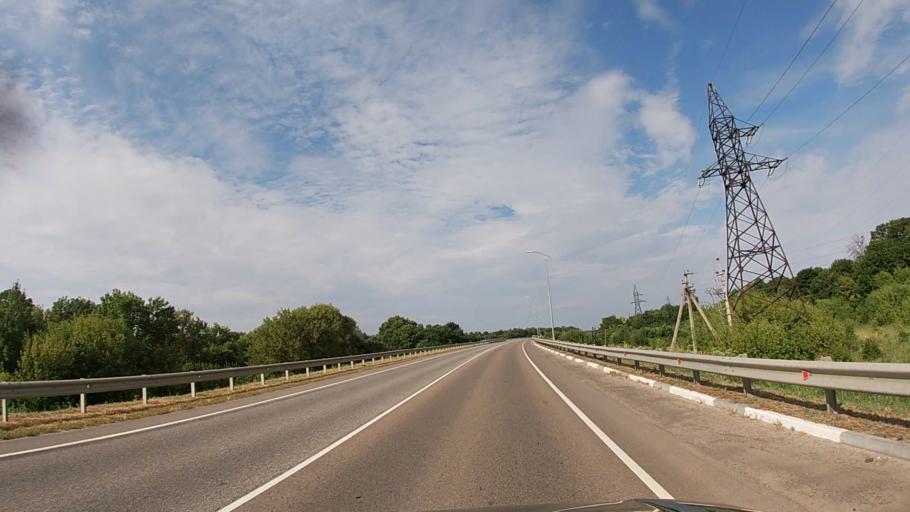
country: RU
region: Belgorod
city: Proletarskiy
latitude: 50.8041
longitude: 35.7395
